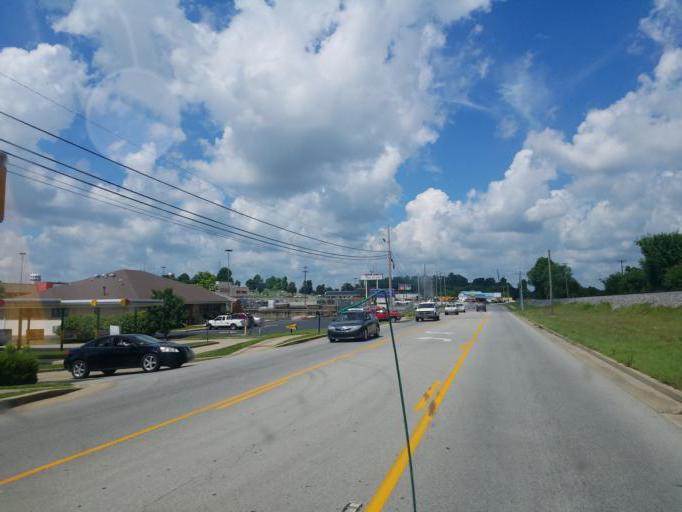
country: US
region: Kentucky
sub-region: Grayson County
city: Leitchfield
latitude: 37.4856
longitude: -86.2724
